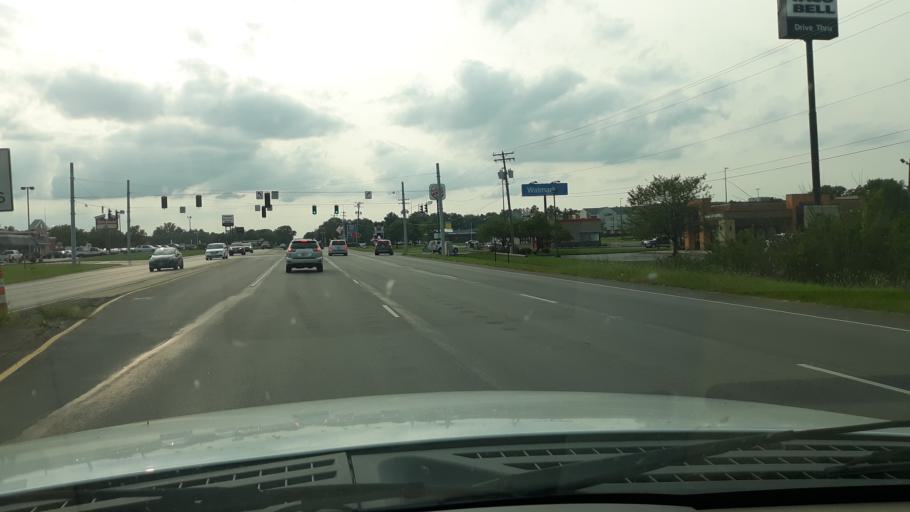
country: US
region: Indiana
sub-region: Gibson County
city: Princeton
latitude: 38.3556
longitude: -87.6038
